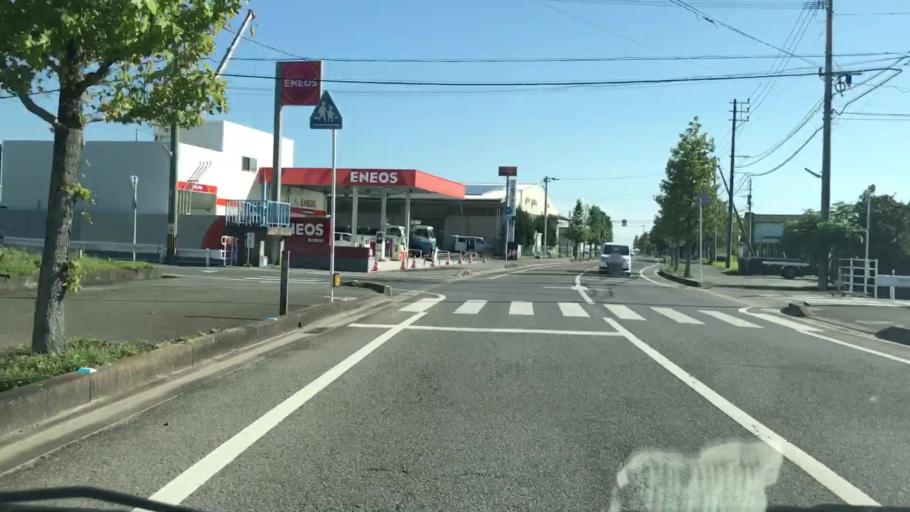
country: JP
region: Saga Prefecture
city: Okawa
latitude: 33.1820
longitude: 130.3136
